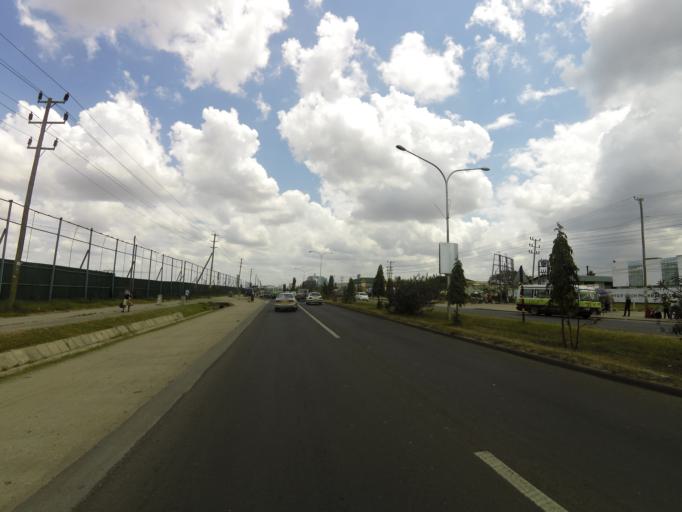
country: TZ
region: Dar es Salaam
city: Dar es Salaam
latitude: -6.8591
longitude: 39.2151
